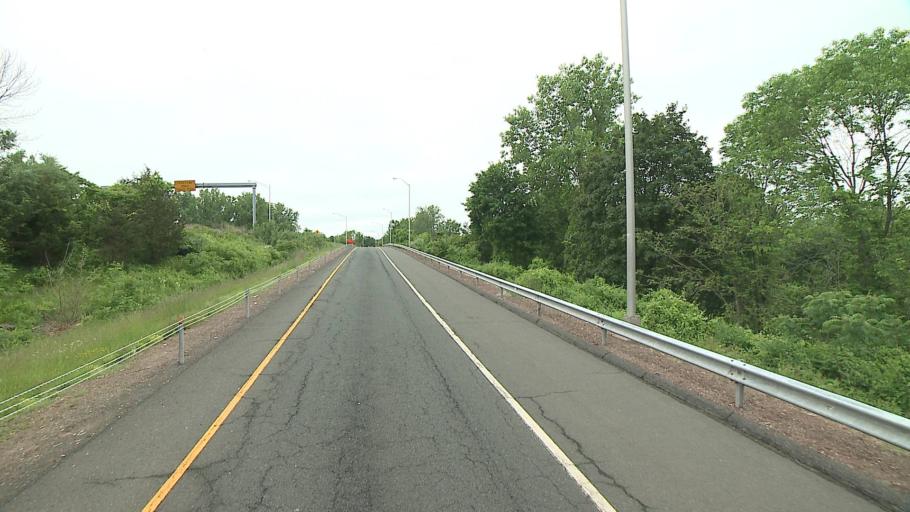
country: US
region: Connecticut
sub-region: Hartford County
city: Wethersfield
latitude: 41.7081
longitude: -72.6467
